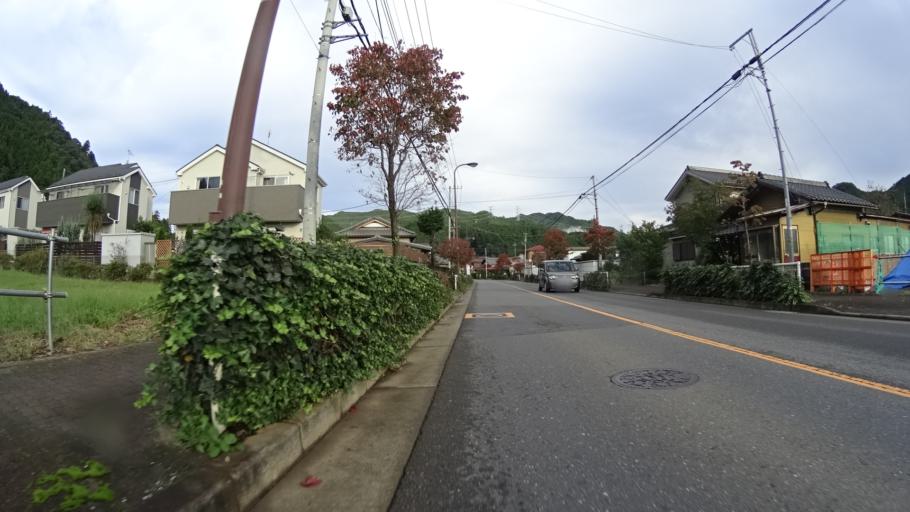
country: JP
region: Tokyo
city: Ome
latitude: 35.8008
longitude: 139.2108
